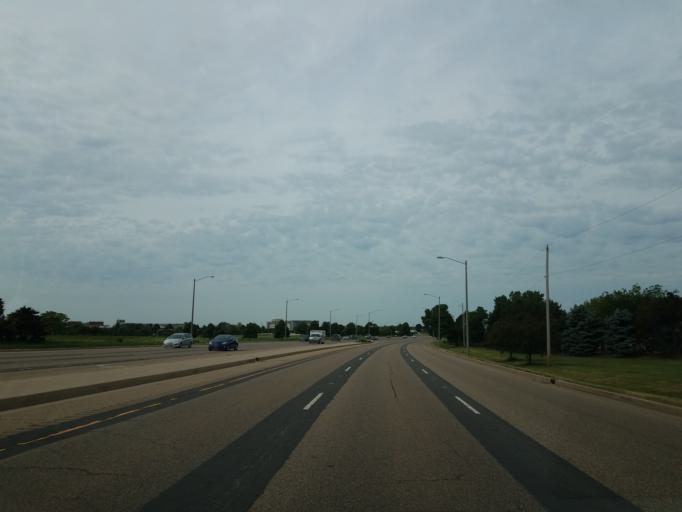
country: US
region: Illinois
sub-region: McLean County
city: Bloomington
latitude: 40.4658
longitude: -88.9556
